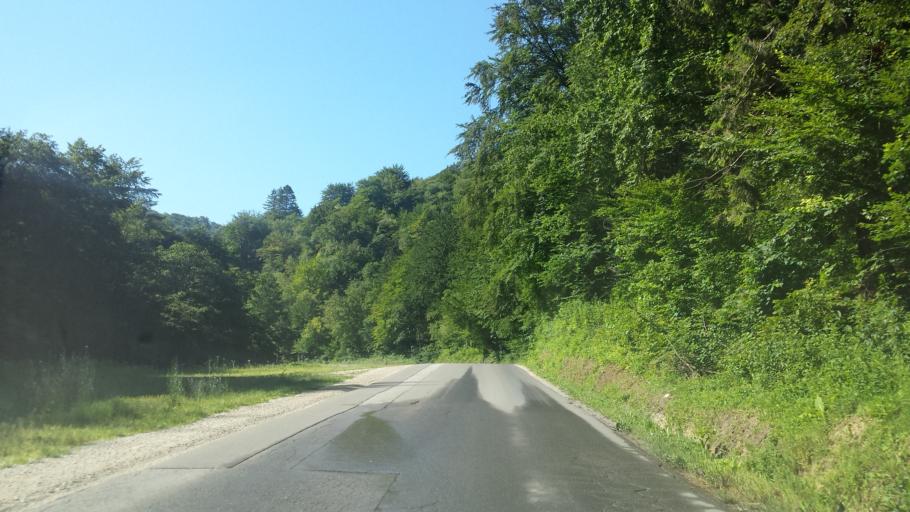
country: HR
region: Zagrebacka
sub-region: Grad Samobor
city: Samobor
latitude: 45.7920
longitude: 15.6917
